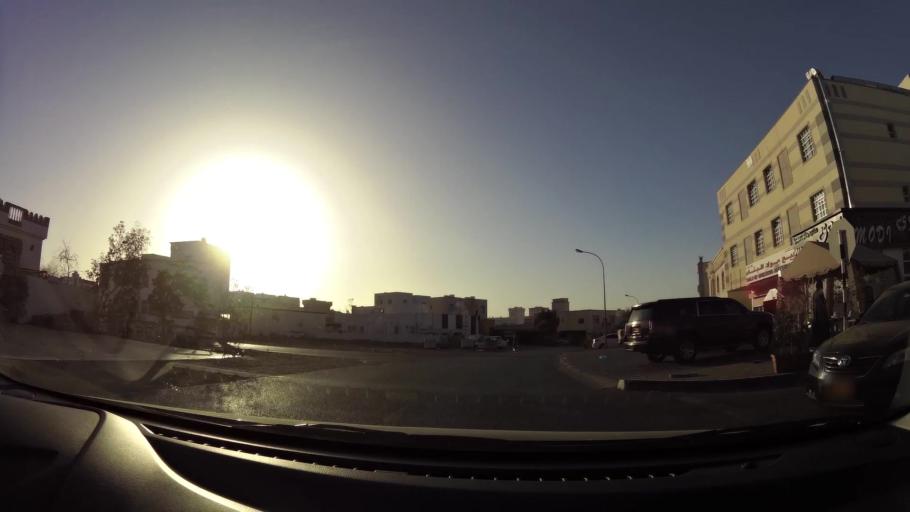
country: OM
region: Muhafazat Masqat
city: As Sib al Jadidah
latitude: 23.6051
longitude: 58.2240
